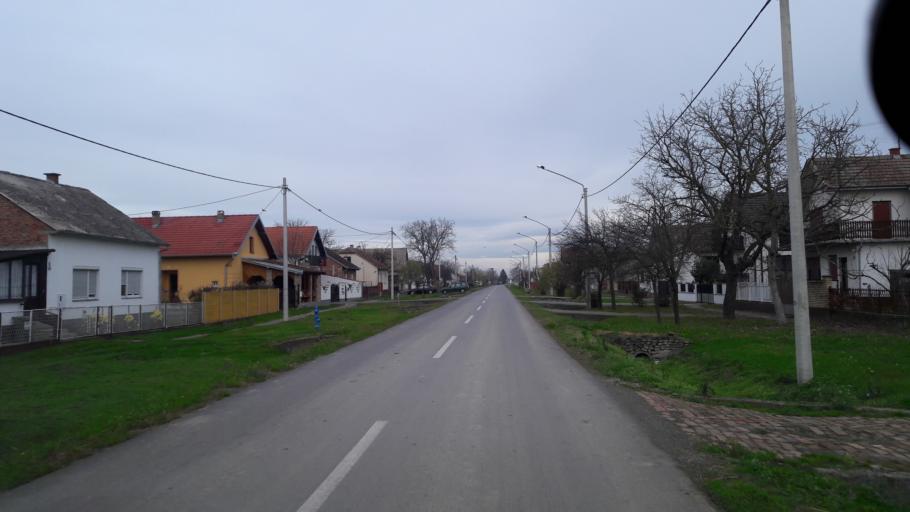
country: HR
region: Osjecko-Baranjska
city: Vladislavci
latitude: 45.4477
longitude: 18.5608
